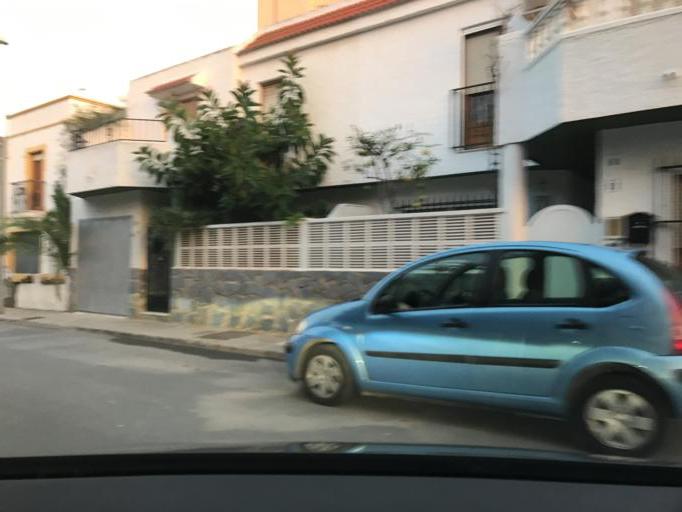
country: ES
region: Andalusia
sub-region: Provincia de Almeria
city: Aguadulce
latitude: 36.8116
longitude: -2.5794
